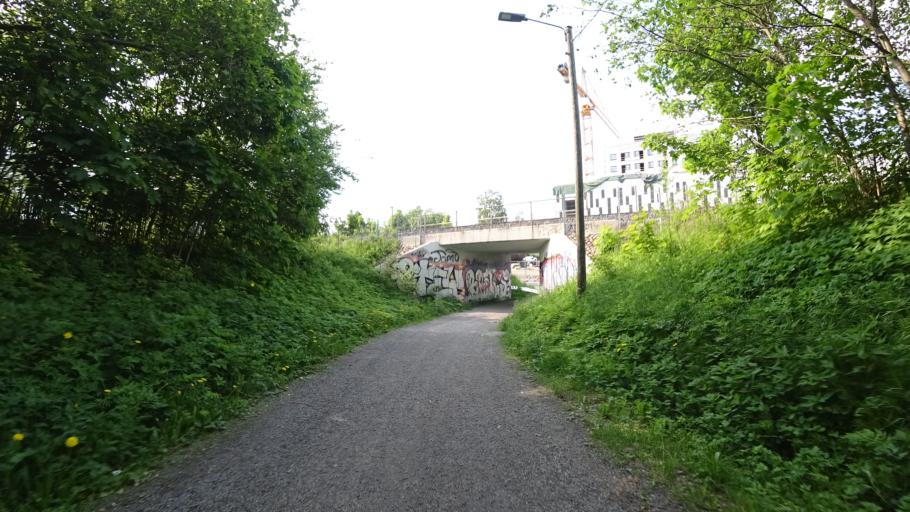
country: FI
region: Pirkanmaa
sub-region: Tampere
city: Pirkkala
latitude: 61.5032
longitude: 23.6301
